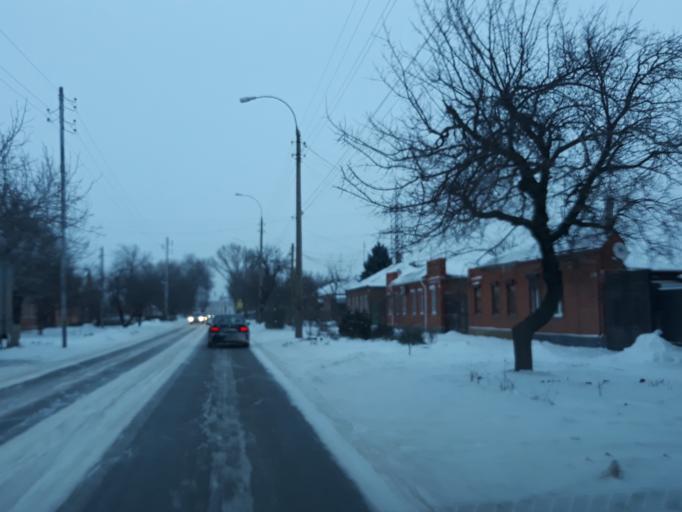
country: RU
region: Rostov
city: Taganrog
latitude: 47.2581
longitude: 38.9389
